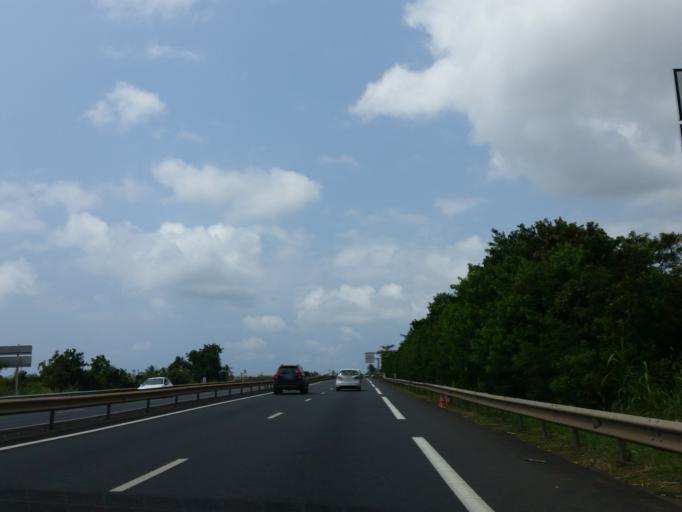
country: RE
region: Reunion
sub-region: Reunion
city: Sainte-Suzanne
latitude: -20.9148
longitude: 55.6131
